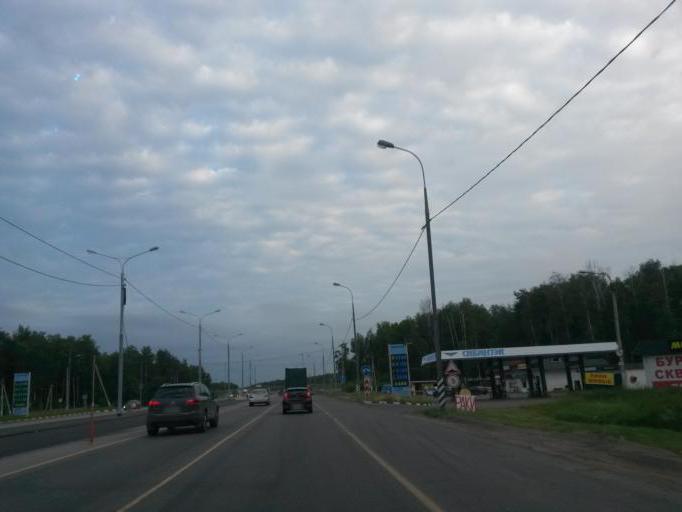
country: RU
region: Moskovskaya
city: Lyubuchany
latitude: 55.1930
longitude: 37.5343
